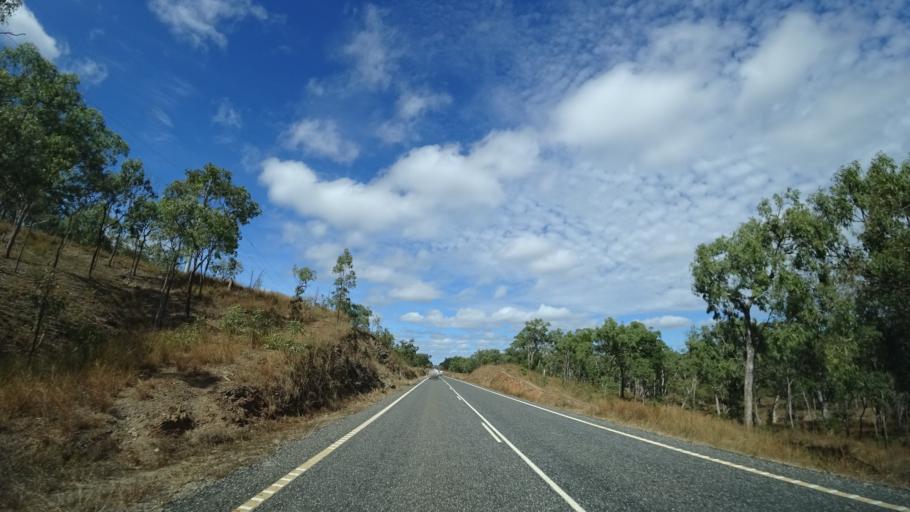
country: AU
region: Queensland
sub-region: Cairns
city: Port Douglas
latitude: -16.3098
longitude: 144.7175
